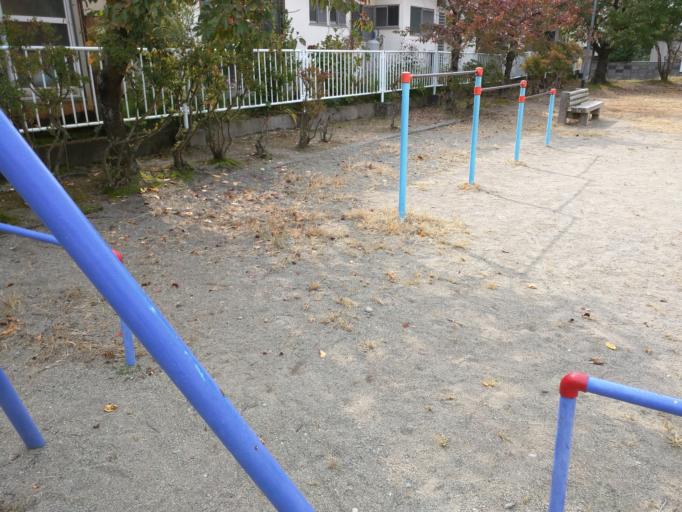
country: JP
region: Fukushima
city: Kitakata
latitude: 37.5057
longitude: 139.9208
